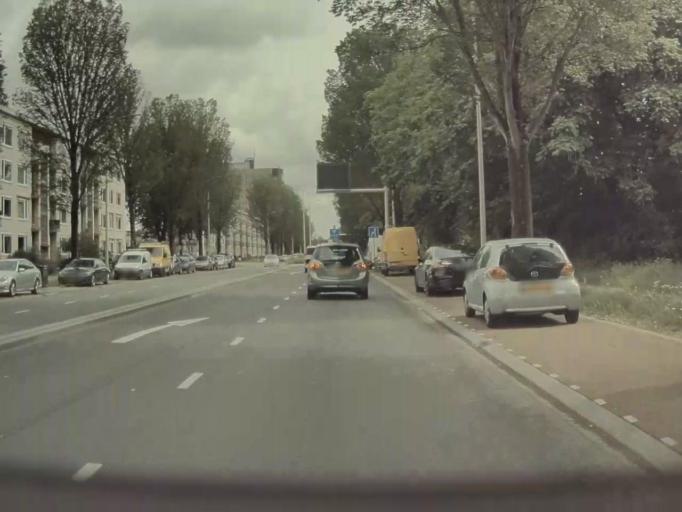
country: NL
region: South Holland
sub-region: Gemeente Den Haag
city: The Hague
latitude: 52.0479
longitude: 4.2946
